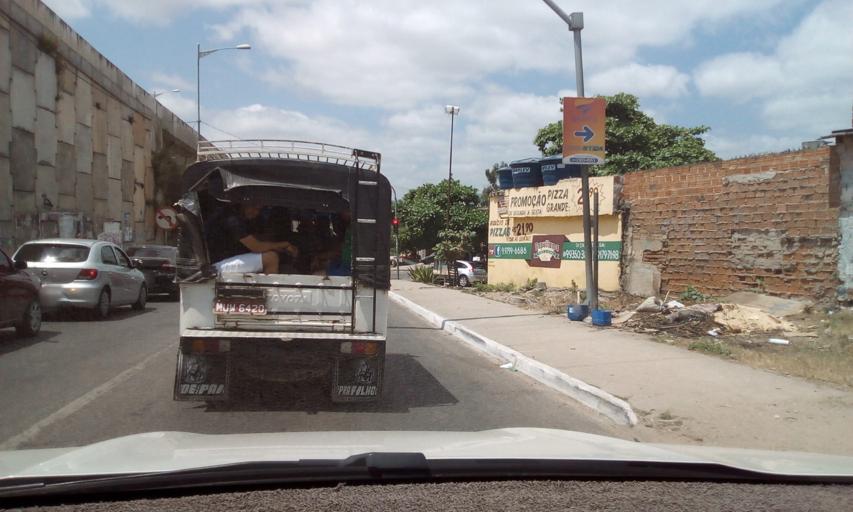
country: BR
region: Pernambuco
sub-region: Caruaru
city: Caruaru
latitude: -8.2877
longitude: -35.9842
